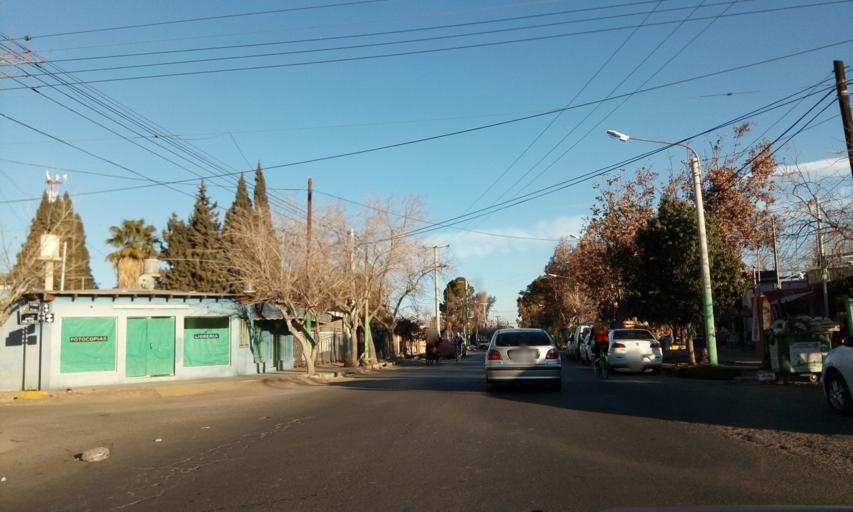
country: AR
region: San Juan
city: San Juan
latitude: -31.5331
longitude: -68.5938
